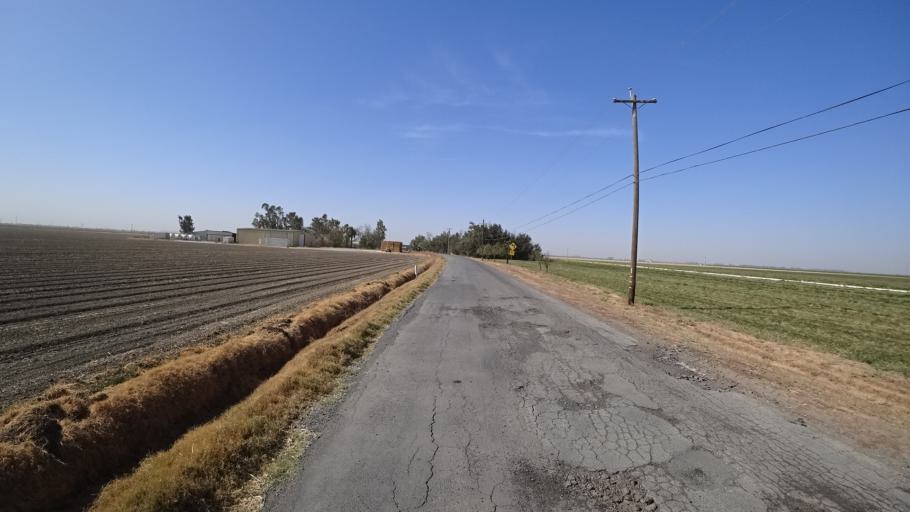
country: US
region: California
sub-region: Yolo County
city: Davis
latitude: 38.5749
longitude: -121.6806
